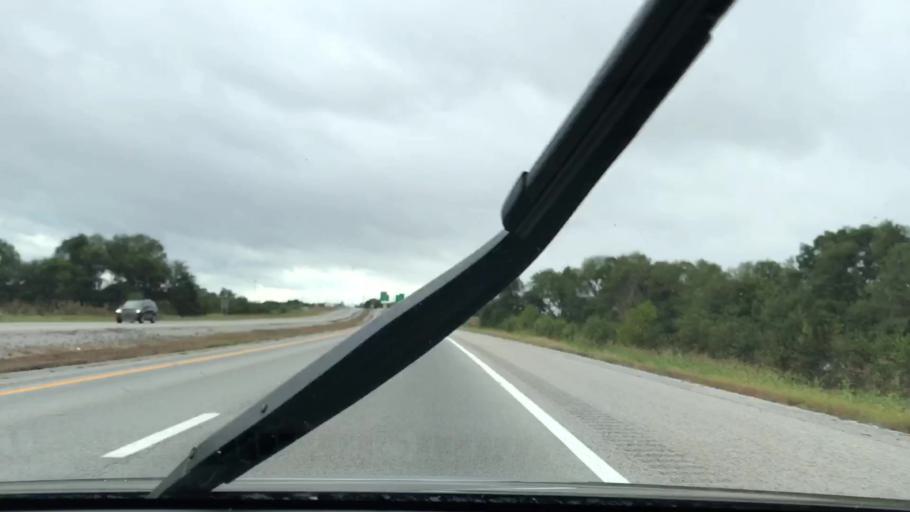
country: US
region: Kentucky
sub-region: Christian County
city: Fort Campbell North
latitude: 36.7523
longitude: -87.5087
